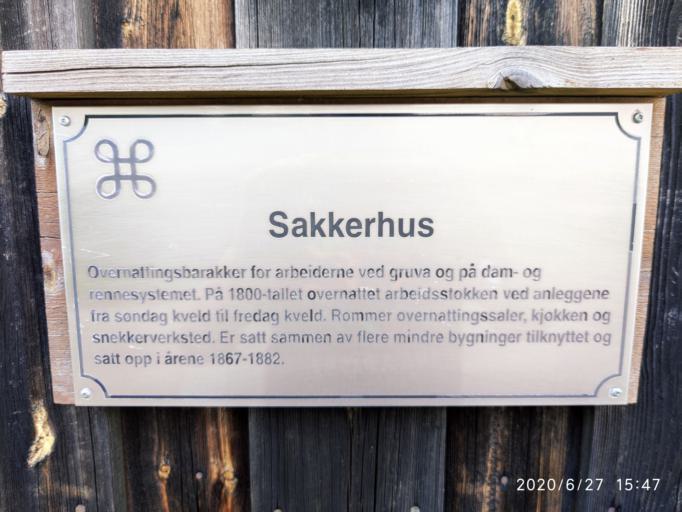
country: NO
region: Buskerud
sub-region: Kongsberg
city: Kongsberg
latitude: 59.6719
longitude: 9.5777
